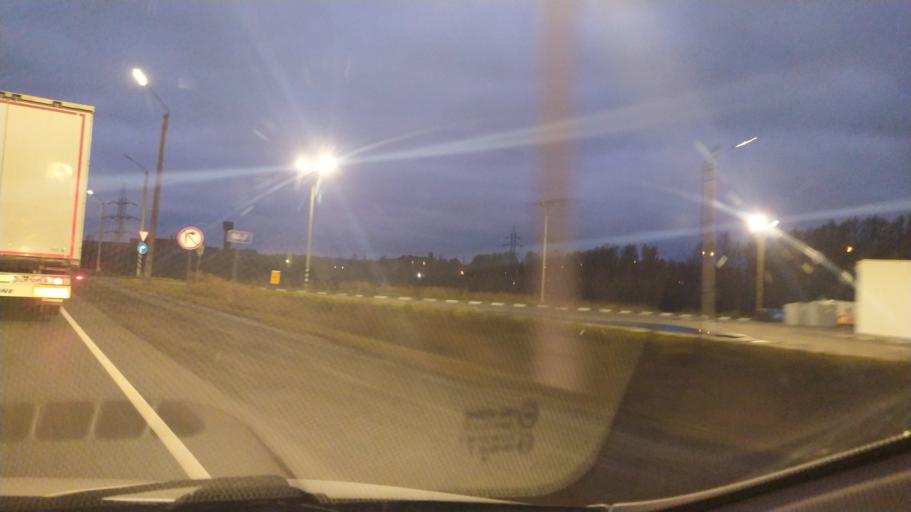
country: RU
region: Chuvashia
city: Kugesi
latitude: 56.0492
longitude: 47.2847
